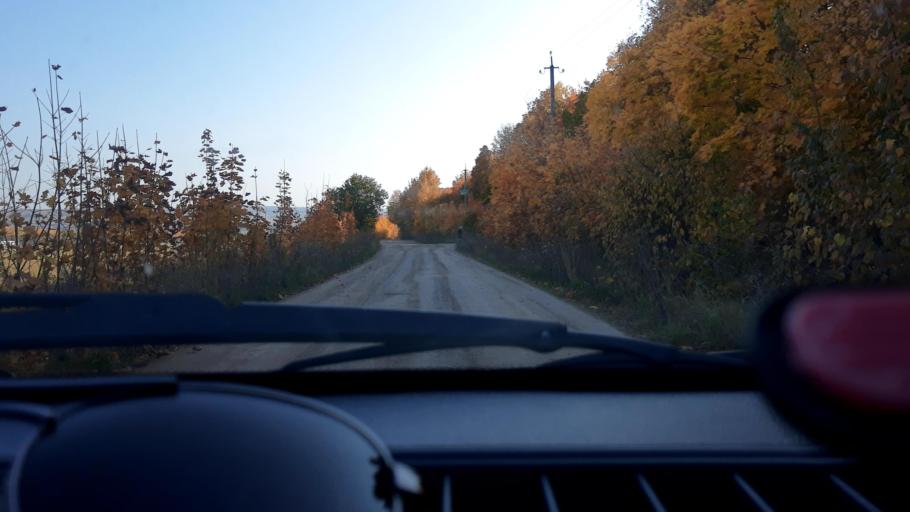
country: RU
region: Bashkortostan
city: Karmaskaly
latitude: 54.3757
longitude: 55.9104
